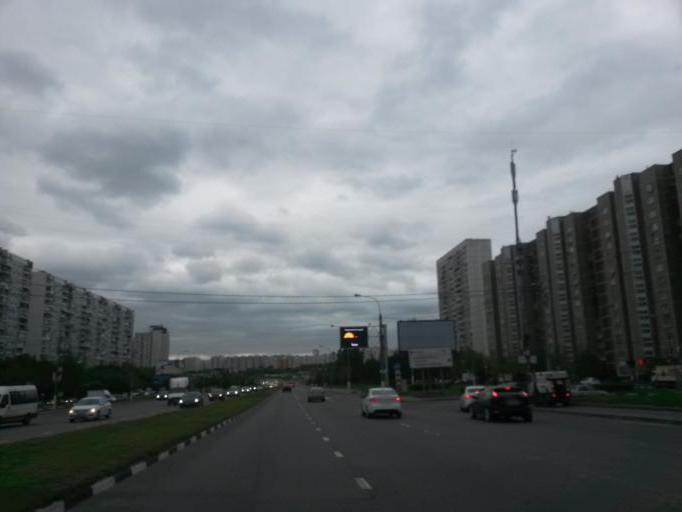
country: RU
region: Moscow
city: Brateyevo
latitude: 55.6356
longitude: 37.7494
